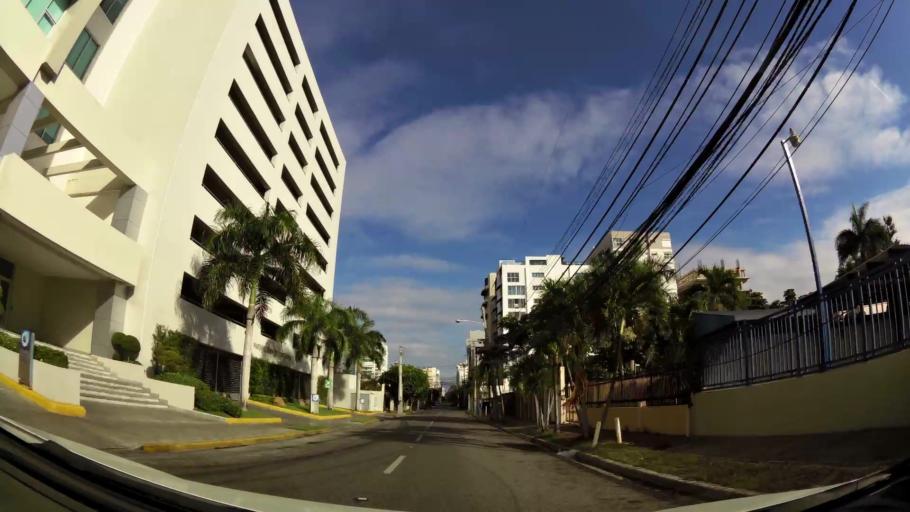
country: DO
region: Nacional
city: La Julia
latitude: 18.4652
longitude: -69.9326
